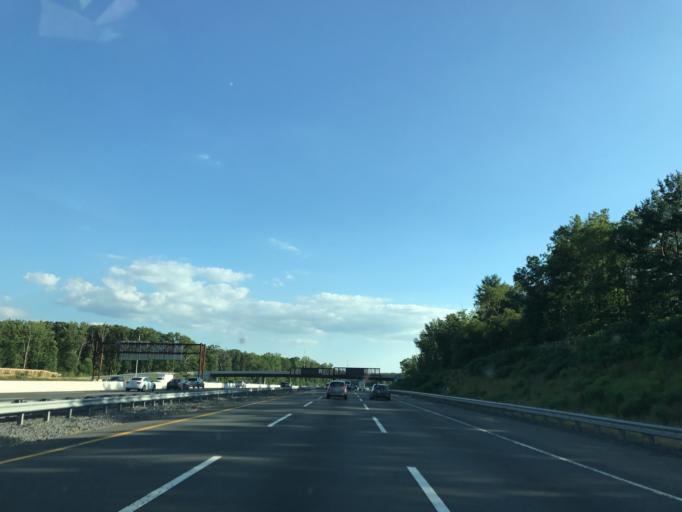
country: US
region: New Jersey
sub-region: Mercer County
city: Hightstown
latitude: 40.2578
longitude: -74.5141
